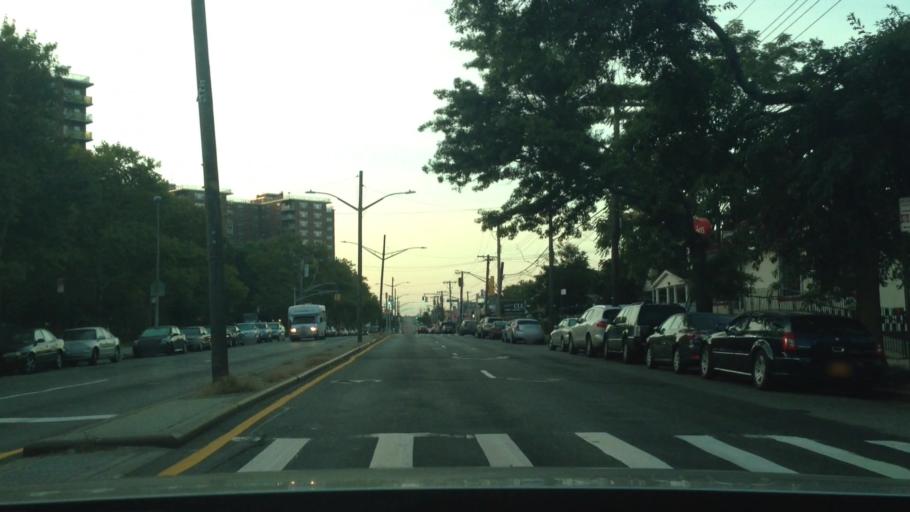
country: US
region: New York
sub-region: Queens County
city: Jamaica
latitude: 40.6744
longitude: -73.7765
